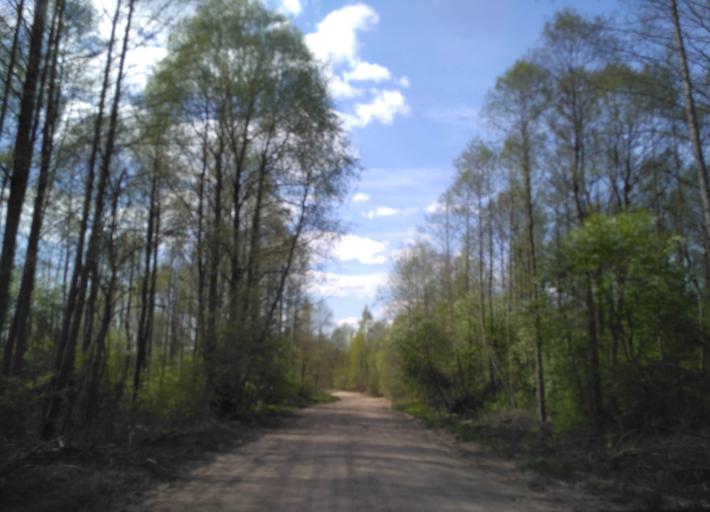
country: BY
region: Minsk
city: Narach
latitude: 54.9855
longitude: 26.6069
